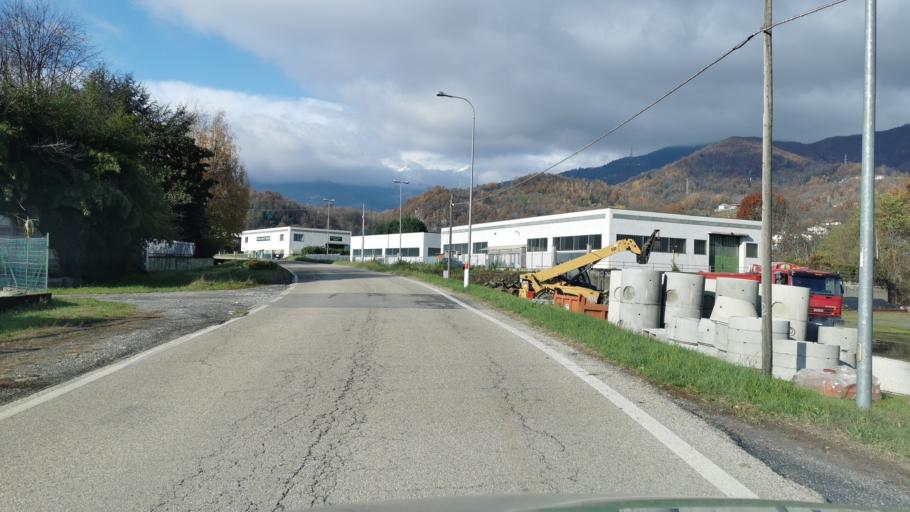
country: IT
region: Piedmont
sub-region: Provincia di Torino
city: Rocca Canavese
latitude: 45.3064
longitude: 7.5812
